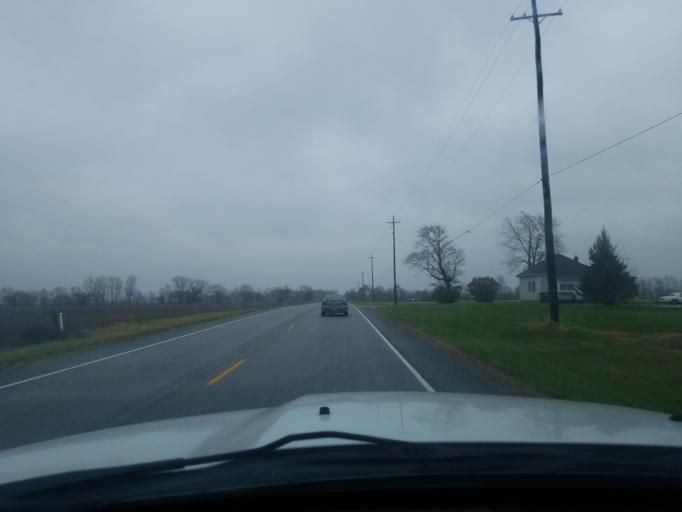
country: US
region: Indiana
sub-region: Howard County
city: Greentown
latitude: 40.4208
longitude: -85.9521
